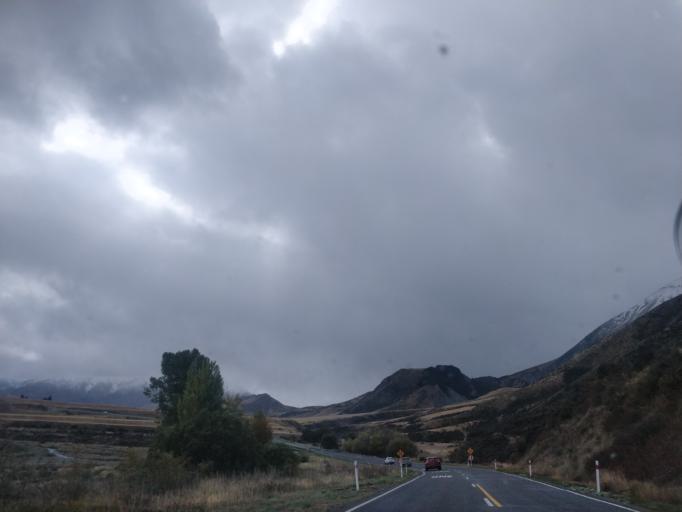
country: NZ
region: Canterbury
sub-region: Ashburton District
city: Methven
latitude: -43.2470
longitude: 171.7232
